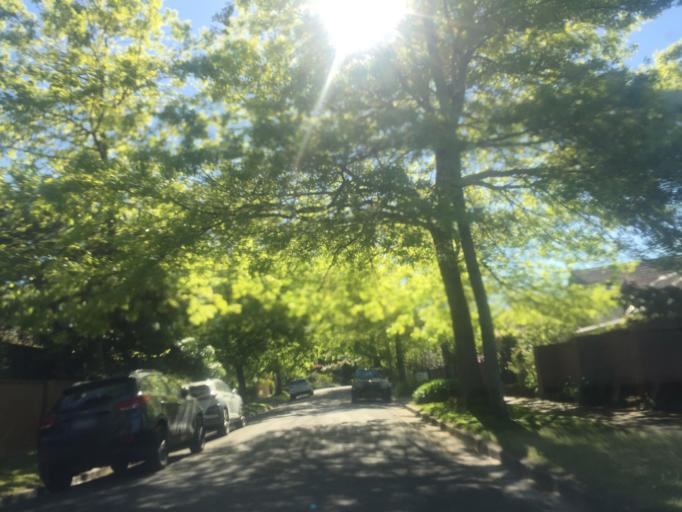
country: AU
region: Victoria
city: Balwyn
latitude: -37.8136
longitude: 145.0763
